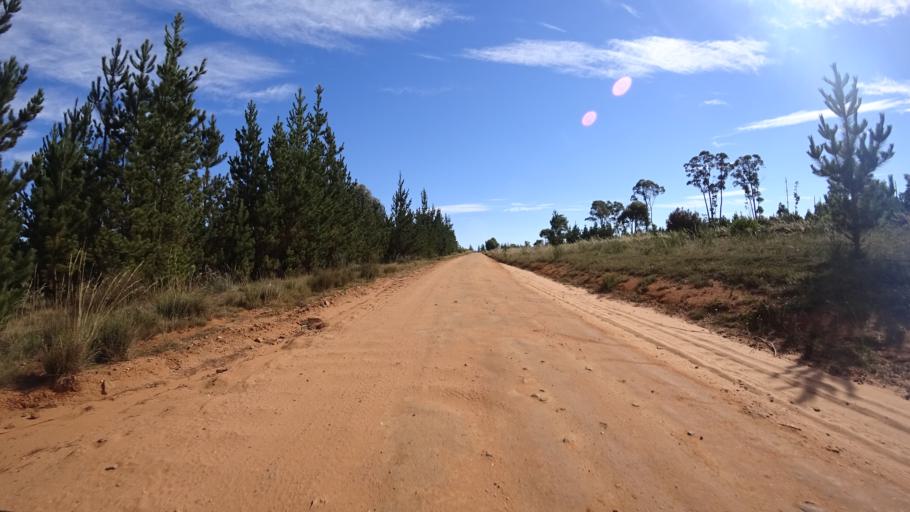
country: AU
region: New South Wales
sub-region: Lithgow
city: Lithgow
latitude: -33.3544
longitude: 150.2527
